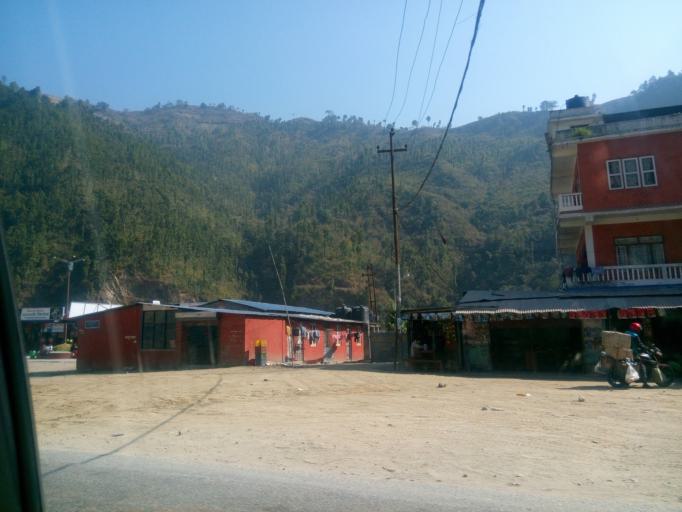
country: NP
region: Central Region
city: Kirtipur
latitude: 27.7630
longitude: 85.0453
